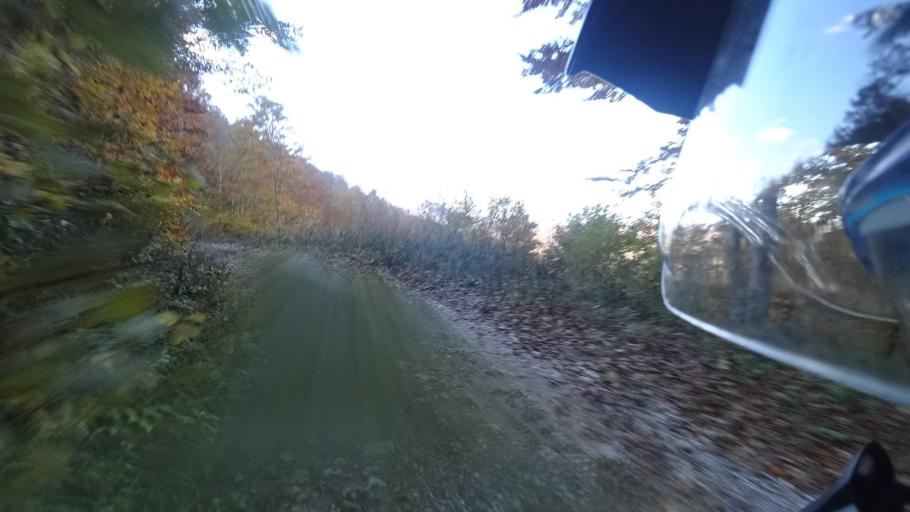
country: HR
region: Karlovacka
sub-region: Grad Ogulin
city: Ogulin
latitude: 45.1779
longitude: 15.1357
